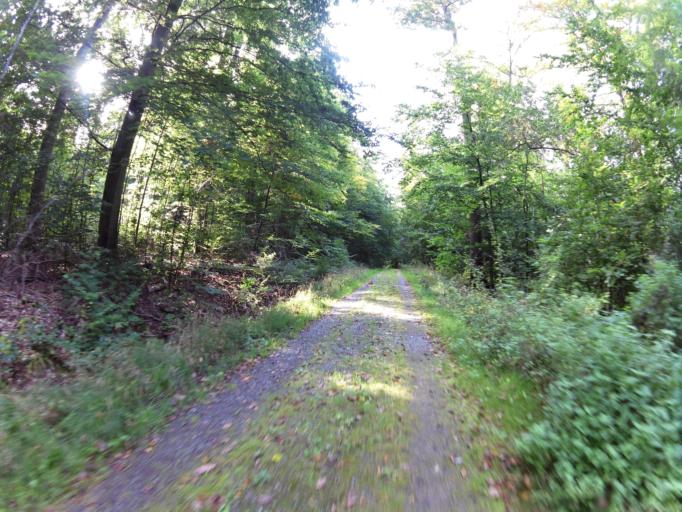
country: DE
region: Bavaria
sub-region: Regierungsbezirk Unterfranken
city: Waldbrunn
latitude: 49.7436
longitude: 9.8062
